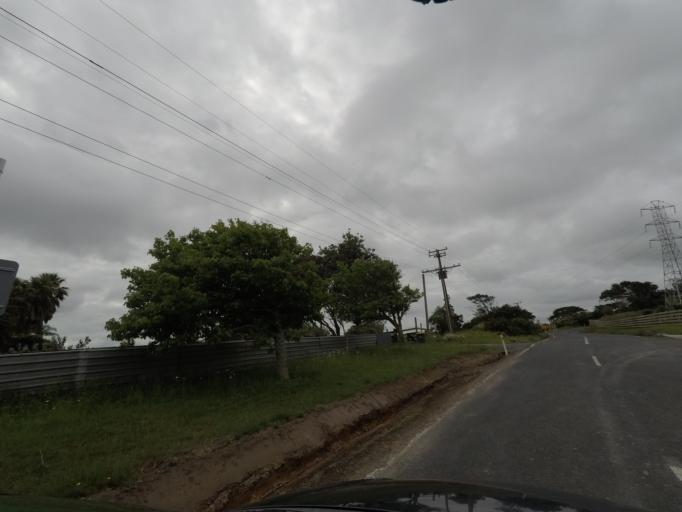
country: NZ
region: Auckland
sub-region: Auckland
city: Rosebank
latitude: -36.8106
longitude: 174.5776
